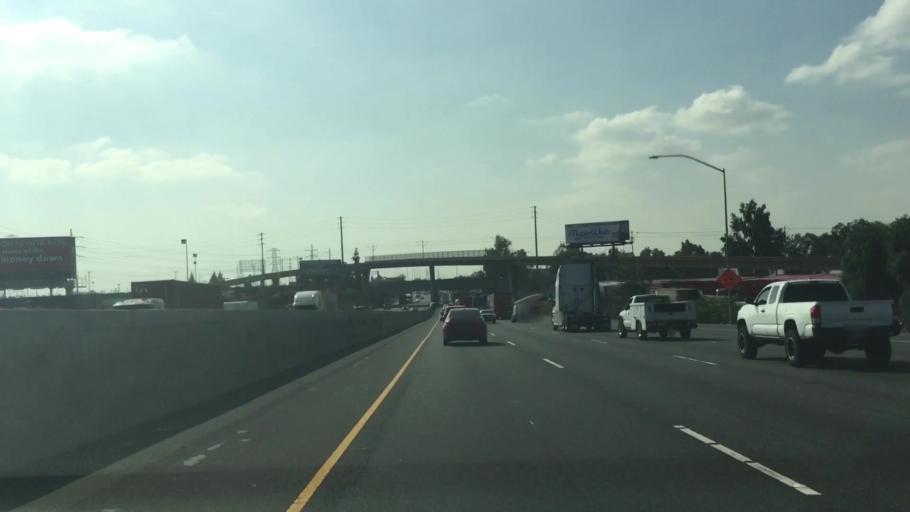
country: US
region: California
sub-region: Los Angeles County
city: Compton
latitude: 33.8431
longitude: -118.2070
